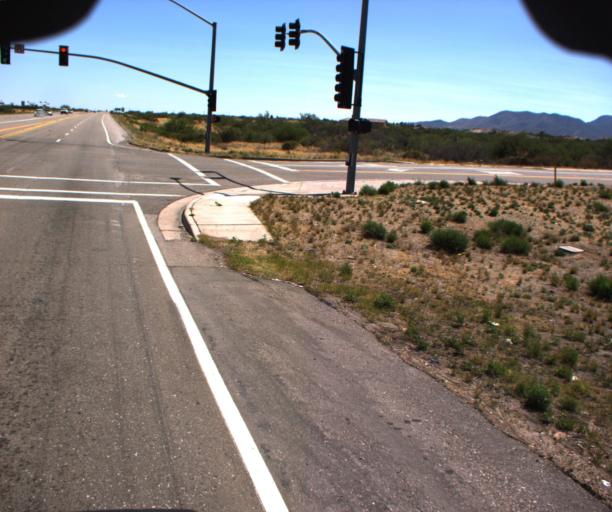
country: US
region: Arizona
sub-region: Cochise County
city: Whetstone
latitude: 31.9619
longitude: -110.3456
